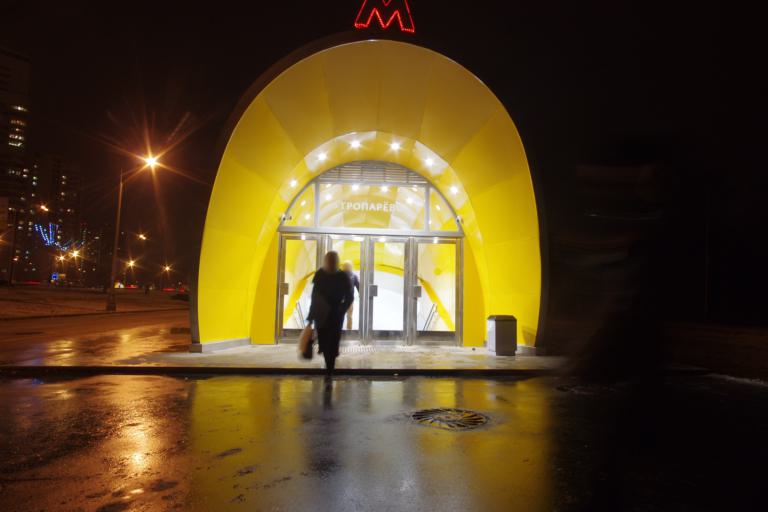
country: RU
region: Moscow
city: Troparevo
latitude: 55.6465
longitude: 37.4743
